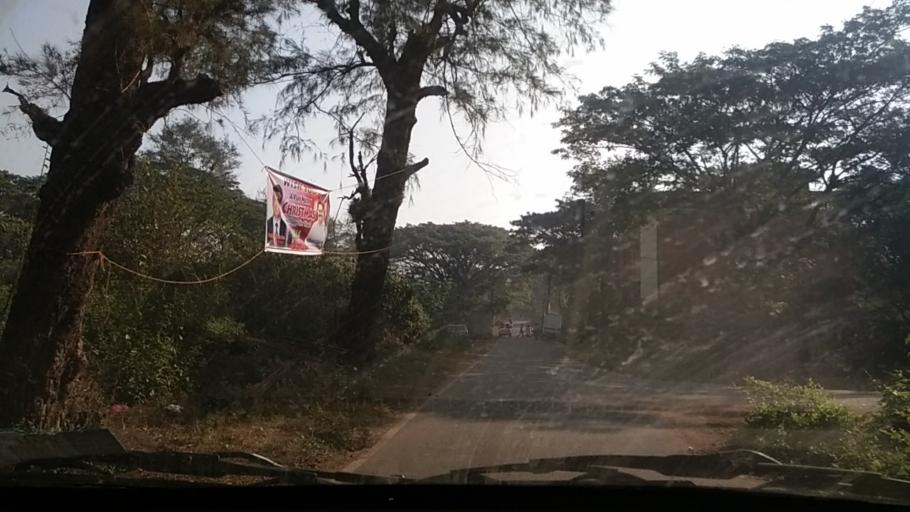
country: IN
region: Goa
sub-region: South Goa
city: Curchorem
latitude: 15.2643
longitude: 74.1117
